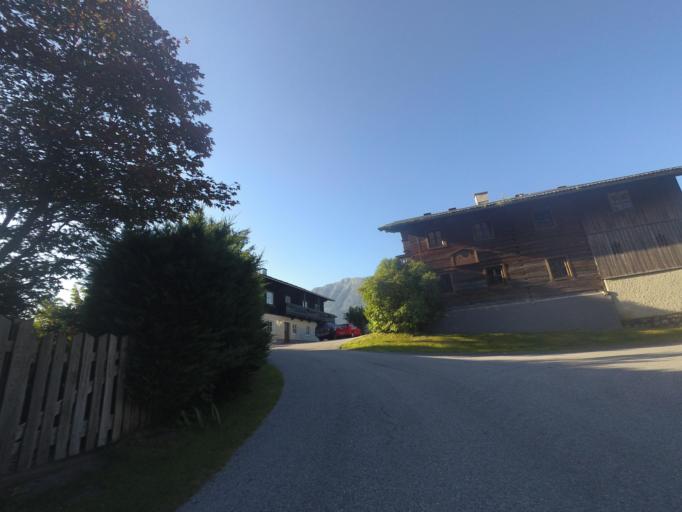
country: AT
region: Salzburg
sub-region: Politischer Bezirk Sankt Johann im Pongau
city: Sankt Veit im Pongau
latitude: 47.3326
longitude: 13.1436
